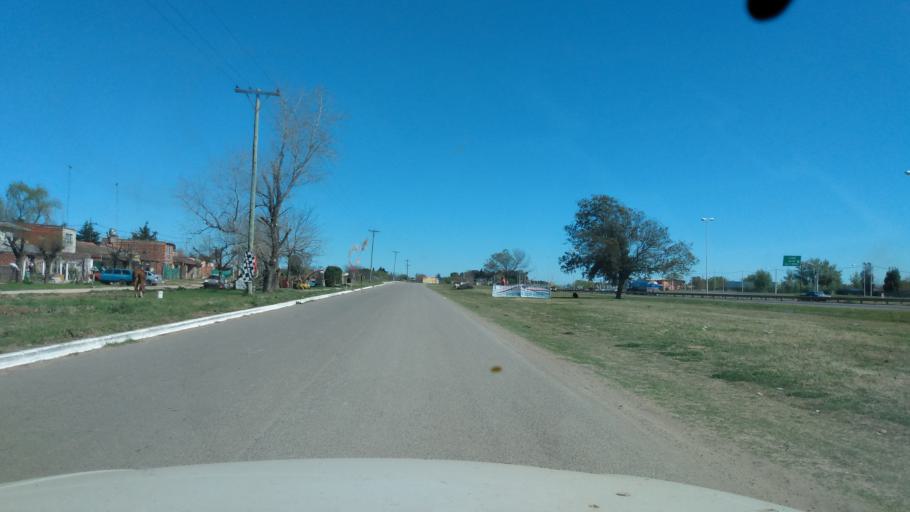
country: AR
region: Buenos Aires
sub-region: Partido de Lujan
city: Lujan
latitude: -34.5646
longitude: -59.0809
